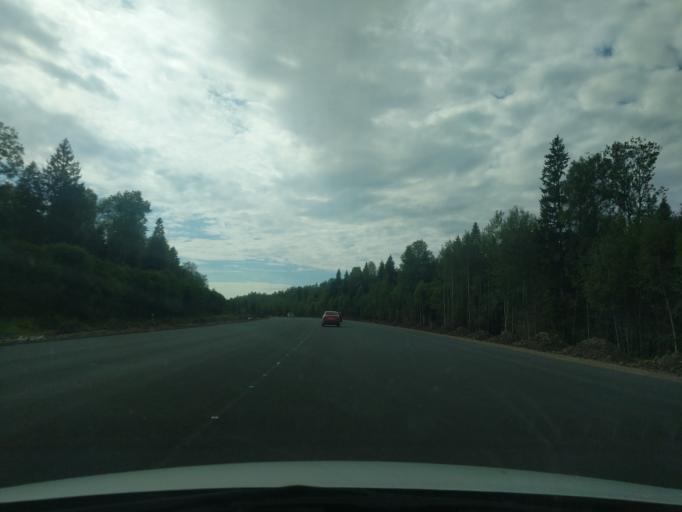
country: RU
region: Kostroma
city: Sudislavl'
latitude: 57.8266
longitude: 41.5049
